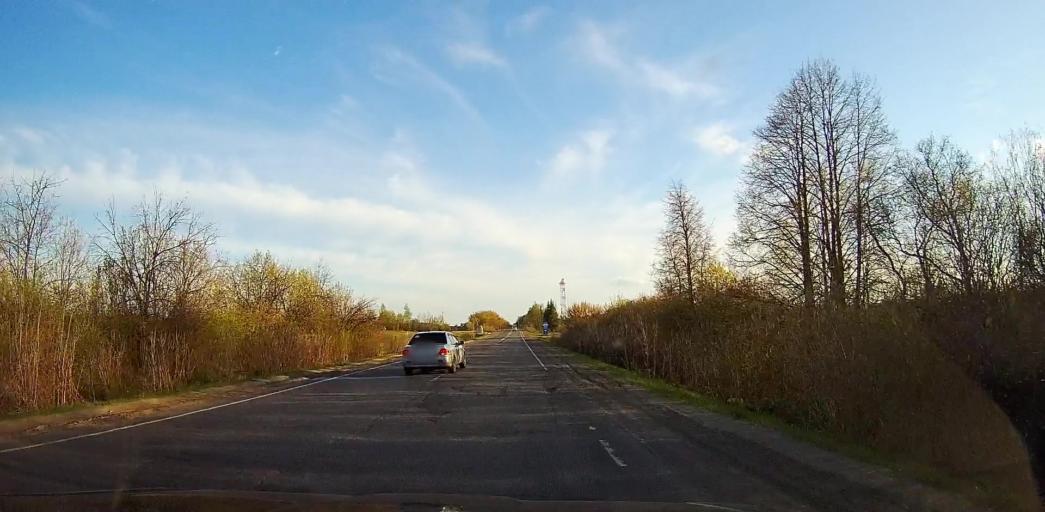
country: RU
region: Moskovskaya
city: Bronnitsy
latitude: 55.3215
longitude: 38.2183
